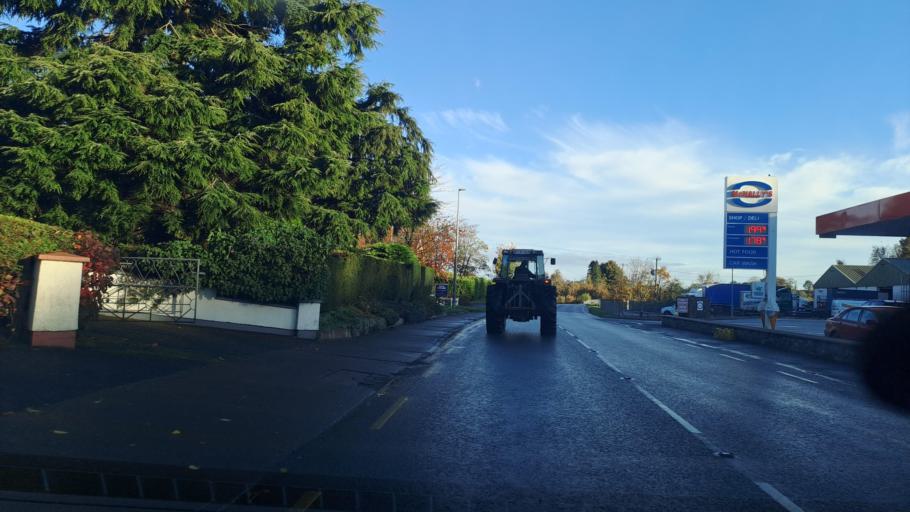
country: IE
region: Ulster
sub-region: County Monaghan
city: Monaghan
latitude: 54.2278
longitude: -6.9710
